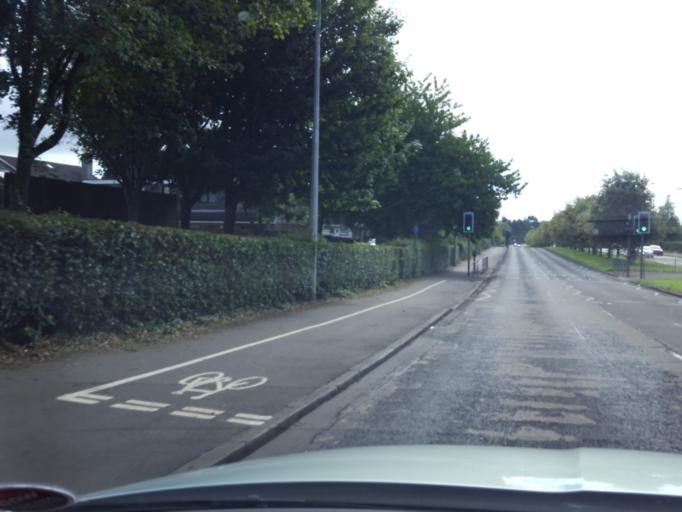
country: GB
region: Scotland
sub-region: Fife
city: Rosyth
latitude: 56.0563
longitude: -3.4398
